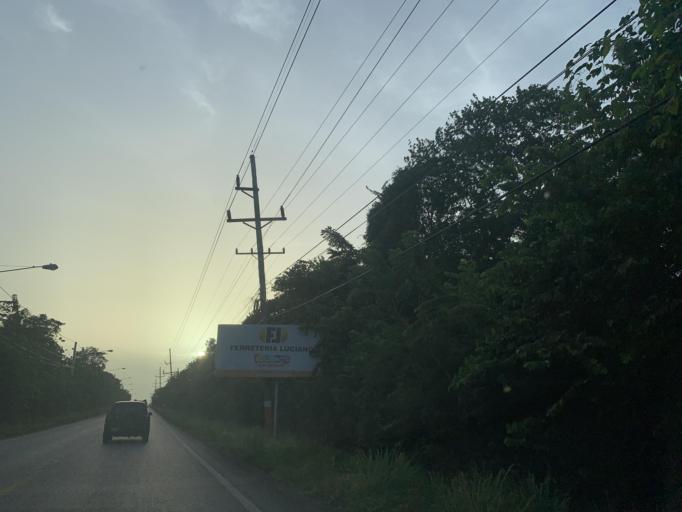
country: DO
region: Puerto Plata
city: Cabarete
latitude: 19.7771
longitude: -70.4716
